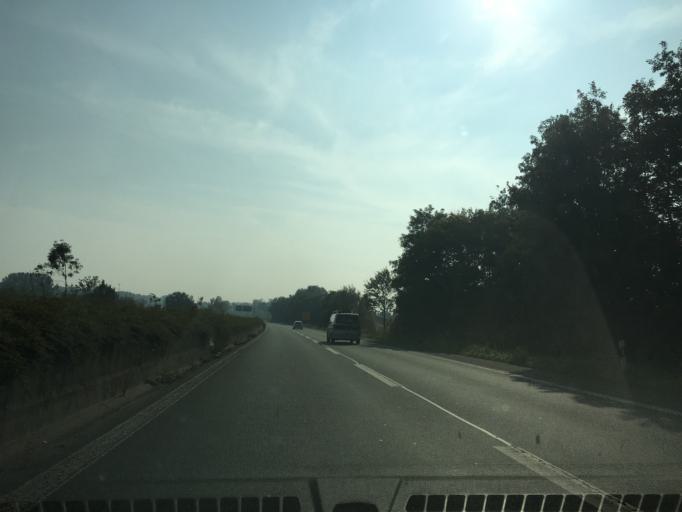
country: DE
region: North Rhine-Westphalia
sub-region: Regierungsbezirk Munster
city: Dulmen
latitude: 51.8493
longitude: 7.2885
